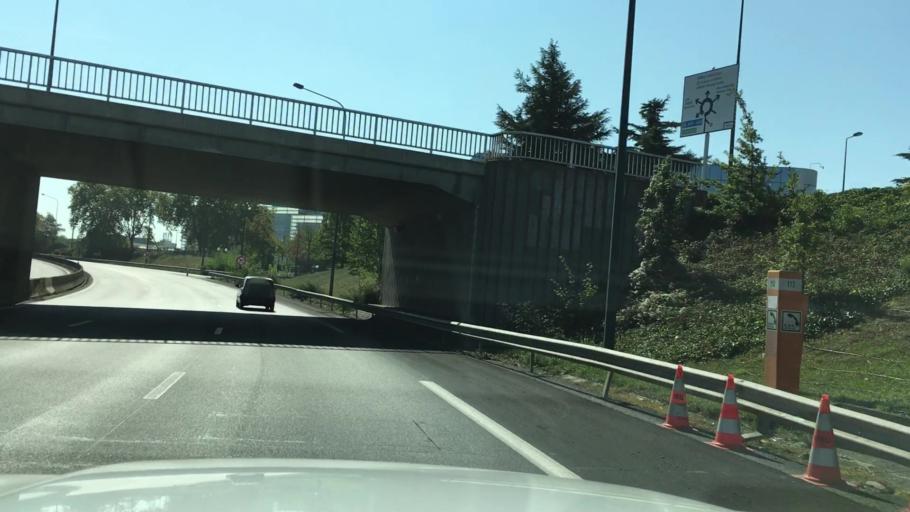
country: FR
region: Midi-Pyrenees
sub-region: Departement de la Haute-Garonne
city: Blagnac
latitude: 43.6266
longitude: 1.3841
